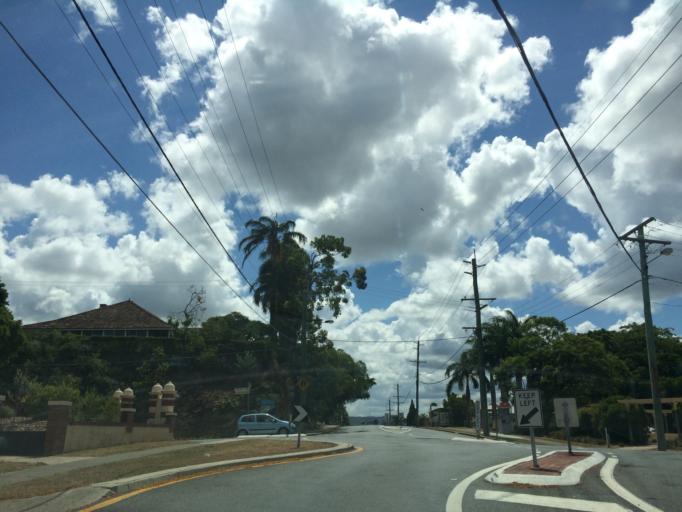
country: AU
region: Queensland
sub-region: Brisbane
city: Woolloongabba
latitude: -27.4839
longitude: 153.0462
